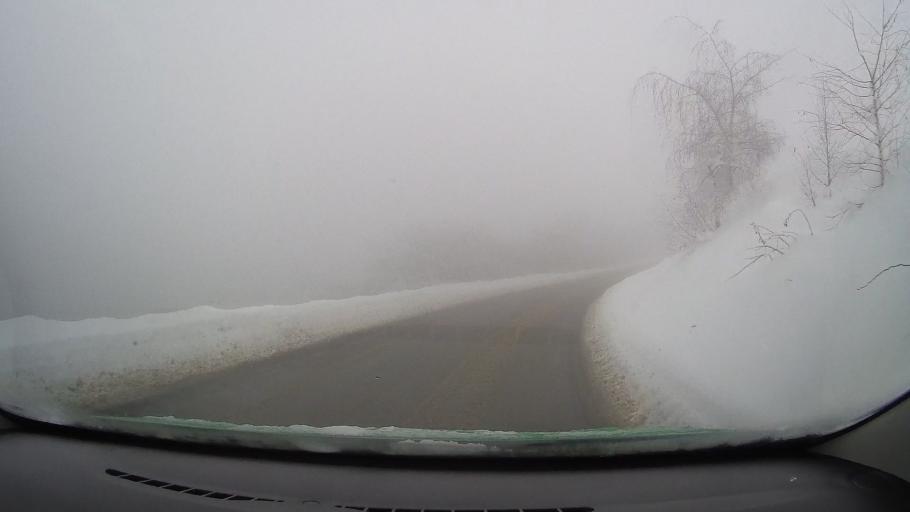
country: RO
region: Sibiu
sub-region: Comuna Poiana Sibiului
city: Poiana Sibiului
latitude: 45.8073
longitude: 23.7469
